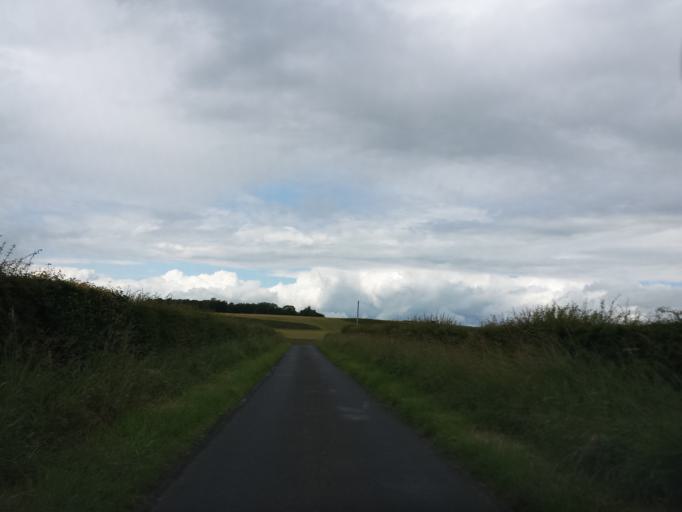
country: GB
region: Scotland
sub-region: The Scottish Borders
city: Saint Boswells
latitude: 55.6028
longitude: -2.5551
